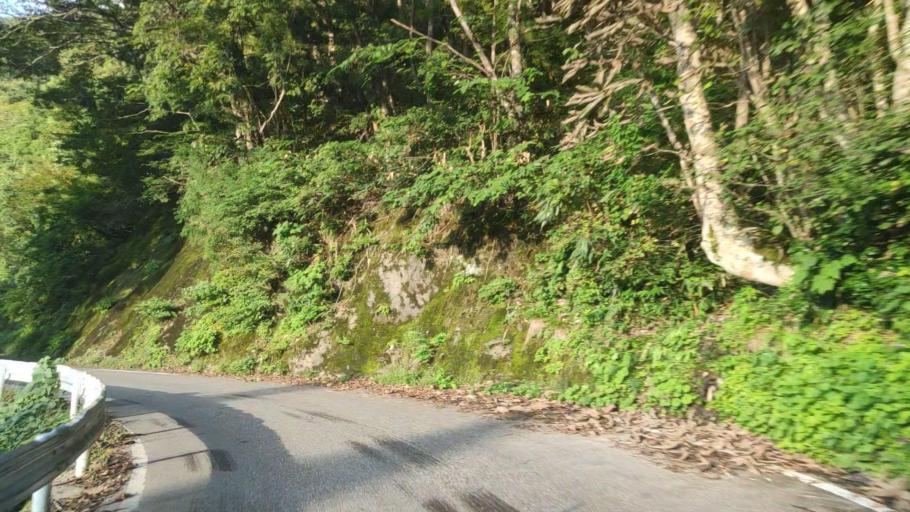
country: JP
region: Toyama
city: Yatsuomachi-higashikumisaka
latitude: 36.4810
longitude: 137.0312
